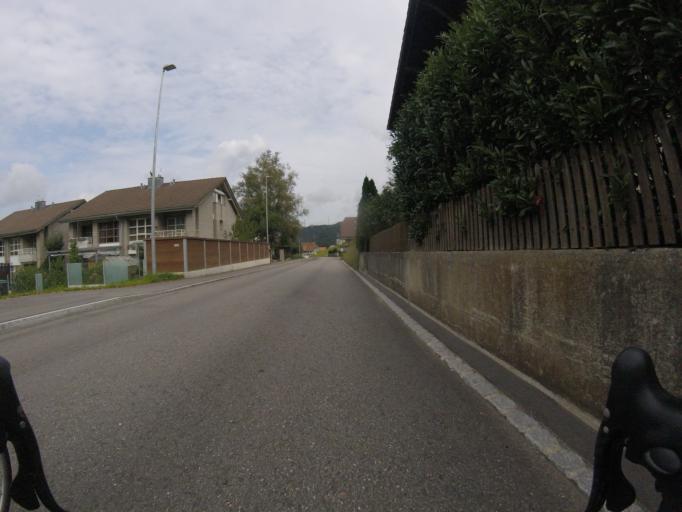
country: CH
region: Bern
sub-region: Emmental District
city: Lutzelfluh
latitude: 47.0012
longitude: 7.6795
